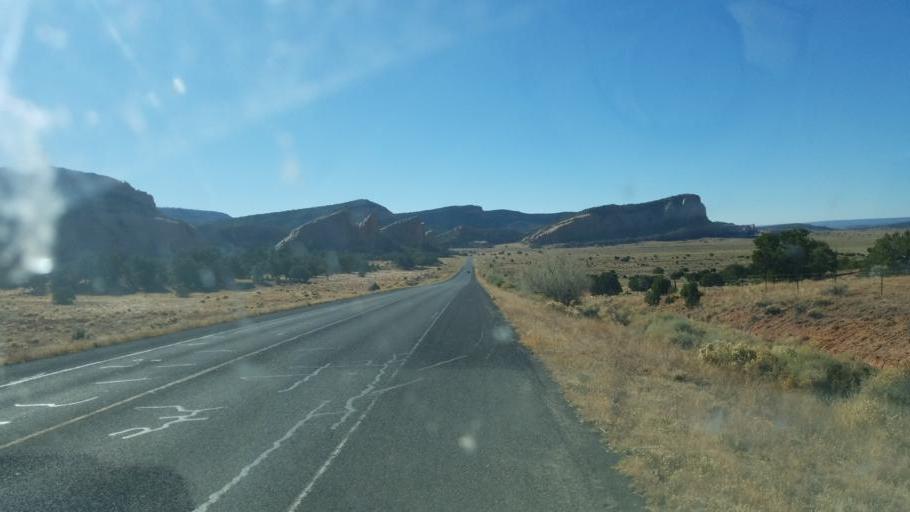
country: US
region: New Mexico
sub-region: McKinley County
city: Navajo
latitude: 35.8567
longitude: -109.0212
